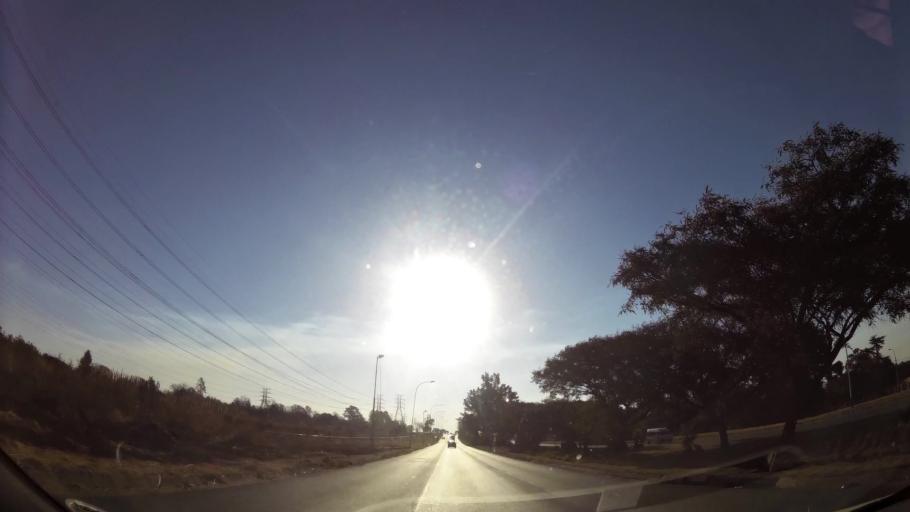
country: ZA
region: Gauteng
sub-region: City of Johannesburg Metropolitan Municipality
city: Roodepoort
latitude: -26.1750
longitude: 27.8779
